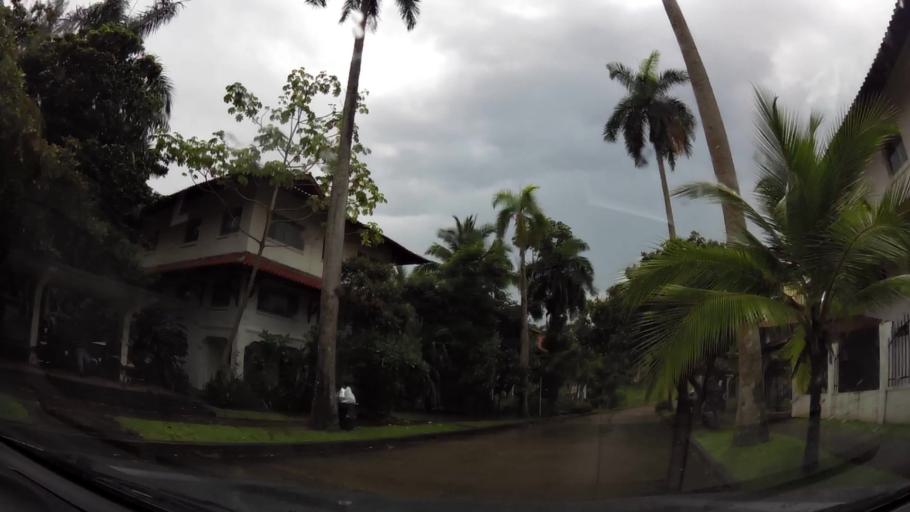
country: PA
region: Panama
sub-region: Distrito de Panama
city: Ancon
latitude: 8.9775
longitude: -79.5594
